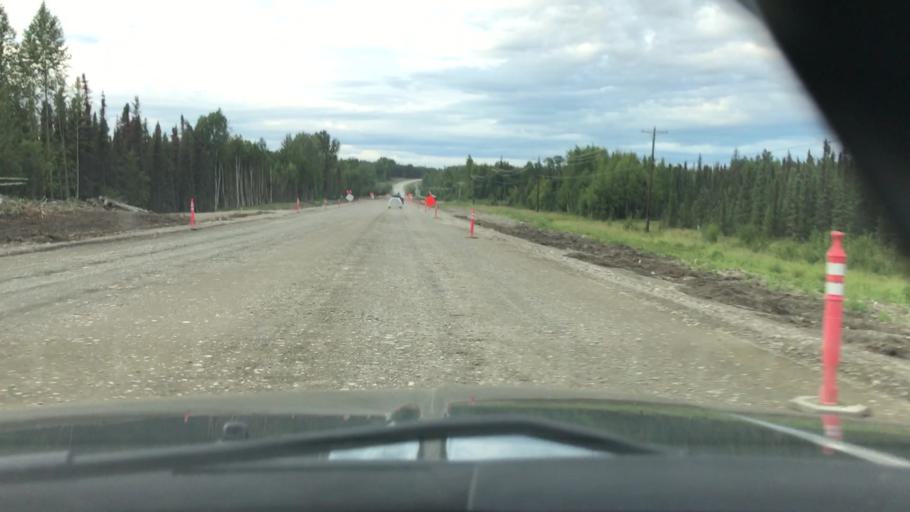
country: US
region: Alaska
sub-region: Matanuska-Susitna Borough
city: Y
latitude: 62.0969
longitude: -150.0616
